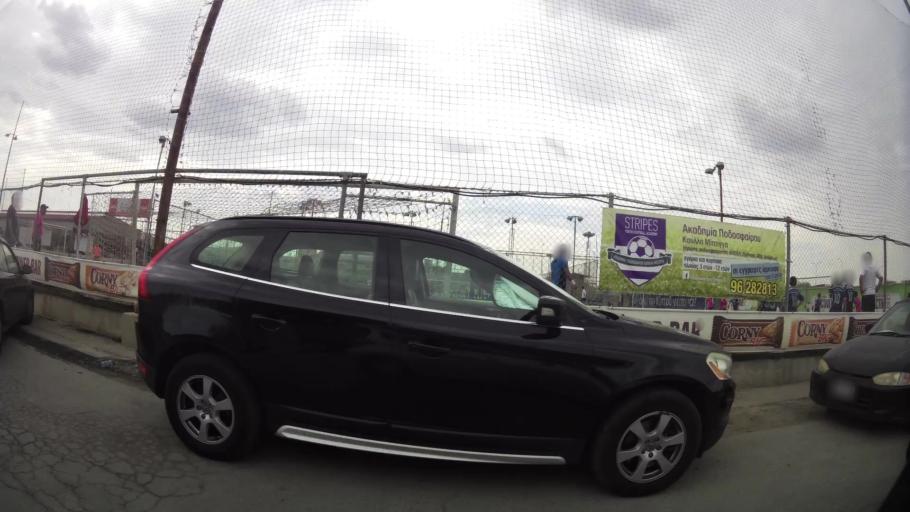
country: CY
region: Lefkosia
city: Geri
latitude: 35.1174
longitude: 33.3651
